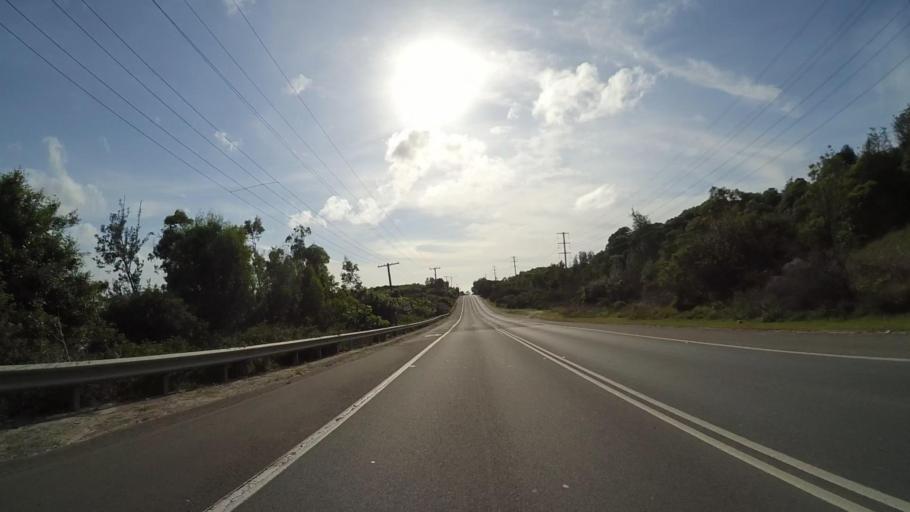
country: AU
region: New South Wales
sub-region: Rockdale
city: Dolls Point
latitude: -34.0238
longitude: 151.1673
